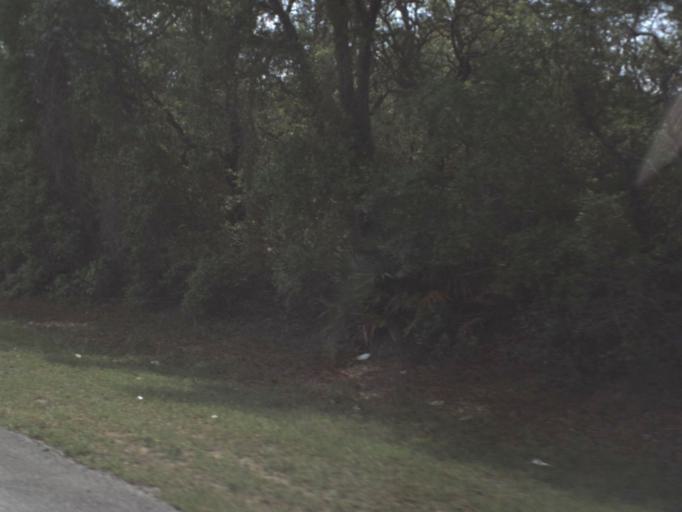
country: US
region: Florida
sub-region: Putnam County
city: Crescent City
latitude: 29.3365
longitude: -81.7229
